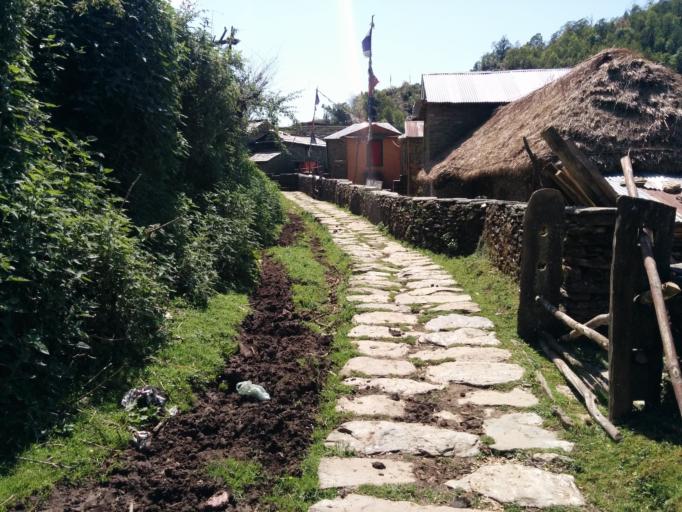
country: NP
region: Western Region
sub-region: Gandaki Zone
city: Pokhara
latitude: 28.2187
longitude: 83.8108
